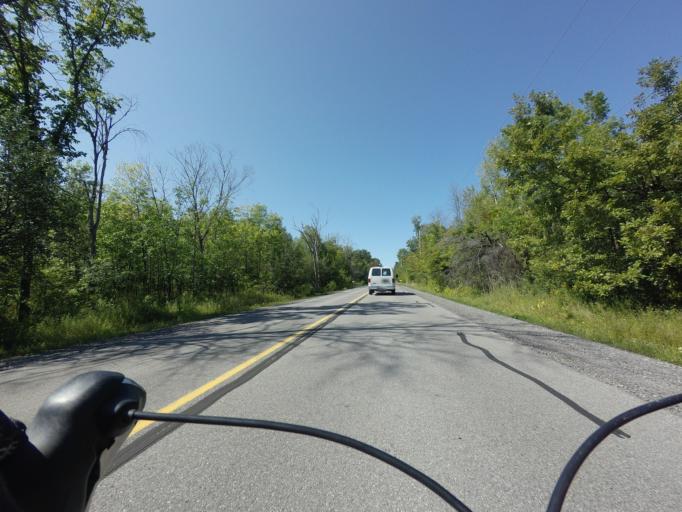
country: CA
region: Ontario
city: Bells Corners
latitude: 45.4054
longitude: -75.9270
